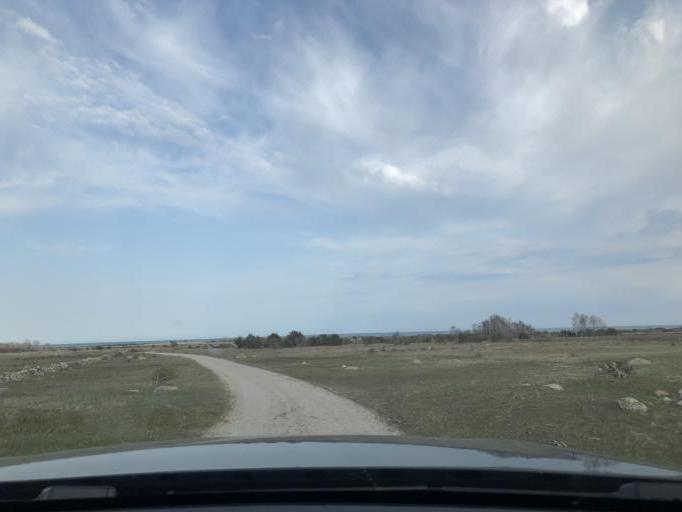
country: SE
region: Kalmar
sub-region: Morbylanga Kommun
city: Sodra Sandby
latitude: 56.5581
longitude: 16.6244
